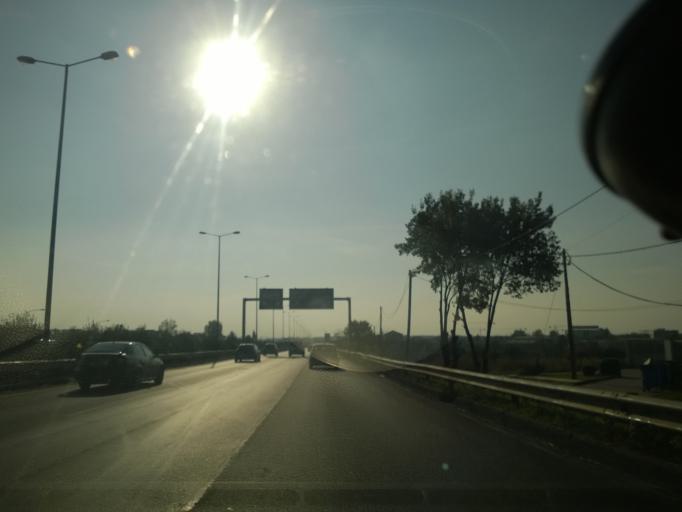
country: GR
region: Central Macedonia
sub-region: Nomos Thessalonikis
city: Pylaia
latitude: 40.5876
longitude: 22.9852
